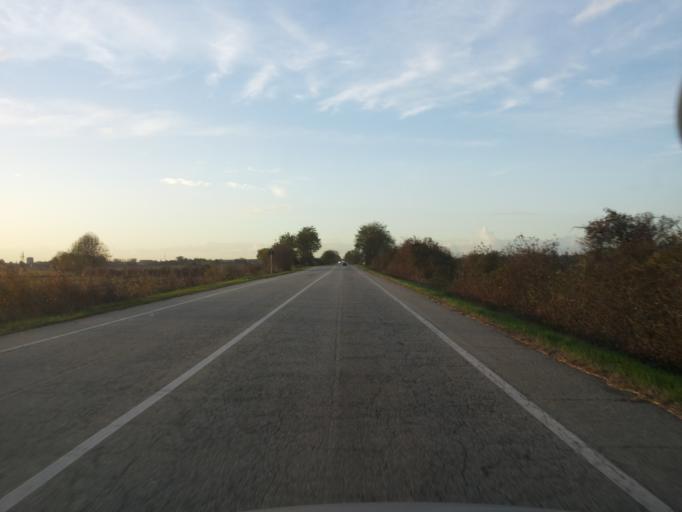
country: IT
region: Piedmont
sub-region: Provincia di Vercelli
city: Trino
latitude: 45.1885
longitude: 8.3296
